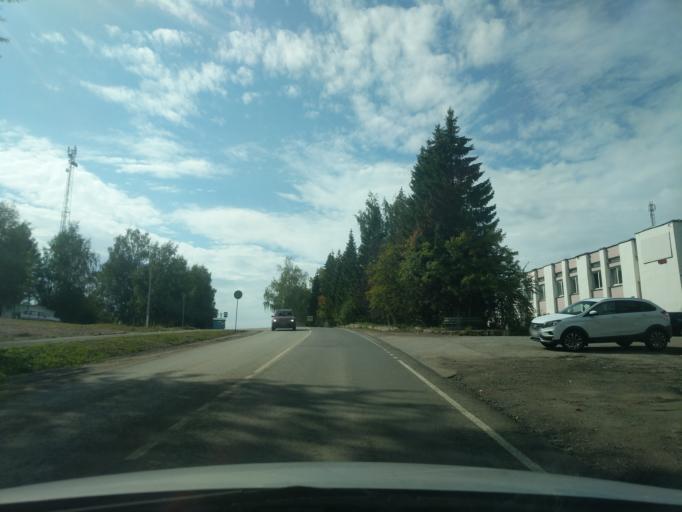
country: RU
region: Kostroma
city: Sudislavl'
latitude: 57.8797
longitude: 41.6894
